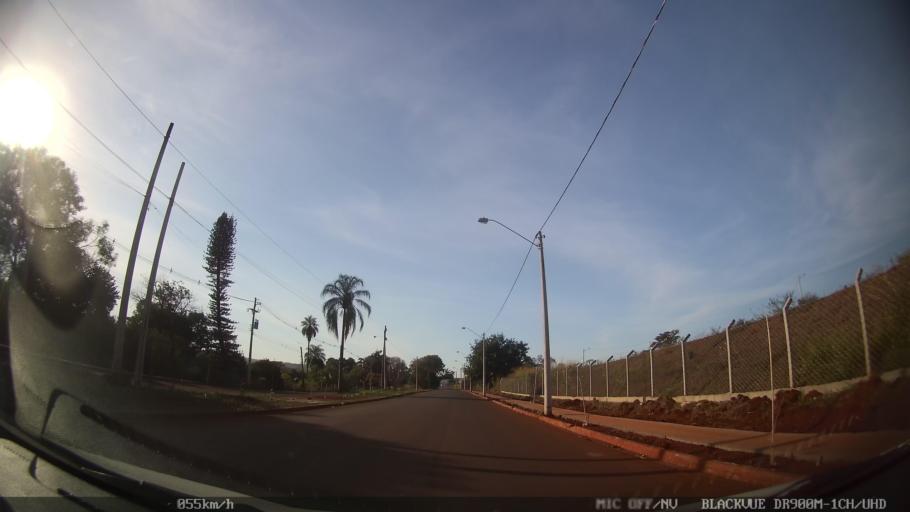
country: BR
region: Sao Paulo
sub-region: Ribeirao Preto
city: Ribeirao Preto
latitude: -21.2744
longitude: -47.8106
